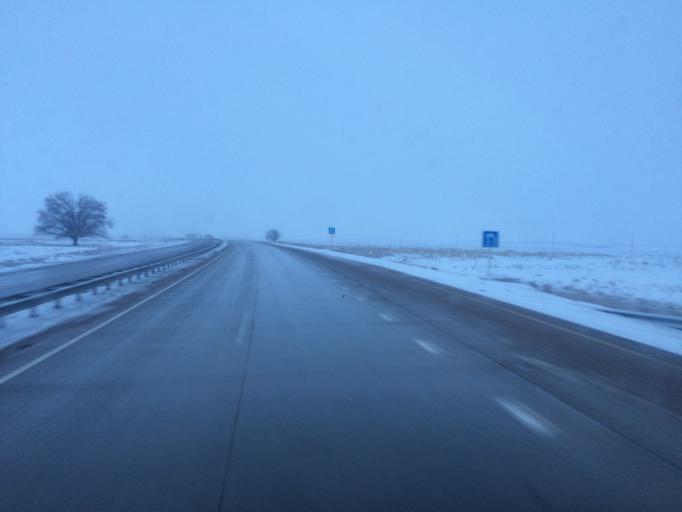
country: KZ
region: Zhambyl
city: Kulan
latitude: 42.9735
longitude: 72.4075
